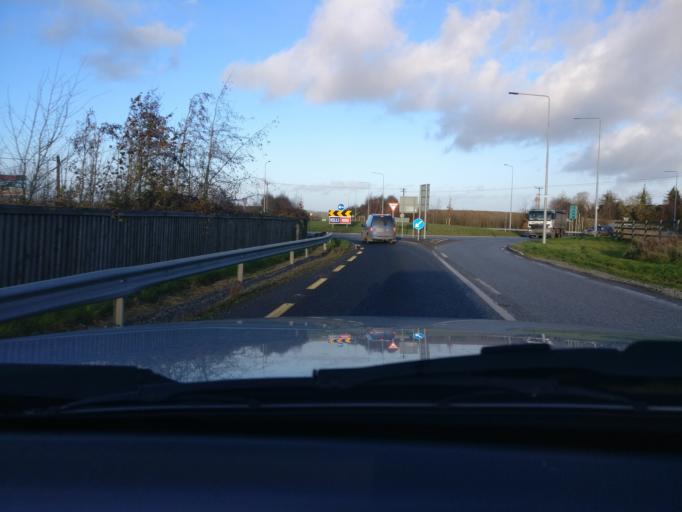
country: IE
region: Leinster
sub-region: An Mhi
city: Kells
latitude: 53.7318
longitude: -6.8921
